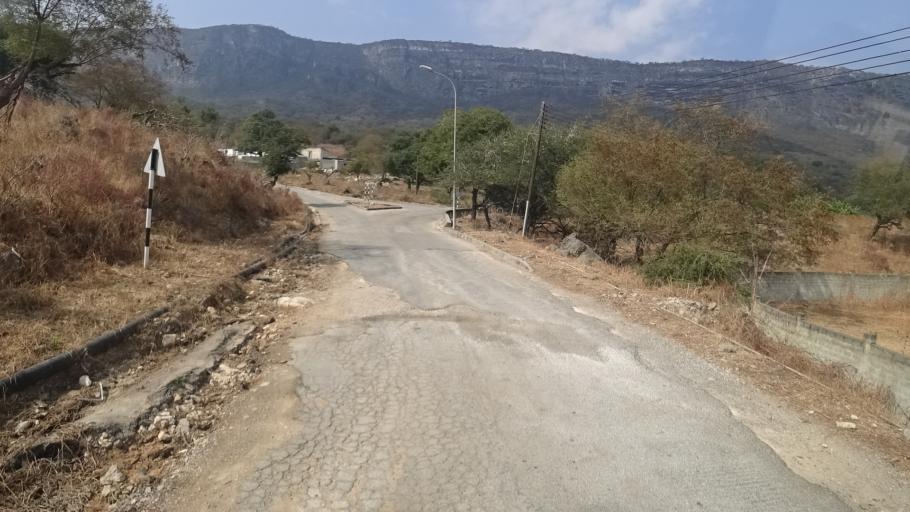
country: YE
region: Al Mahrah
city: Hawf
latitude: 16.7129
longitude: 53.2518
